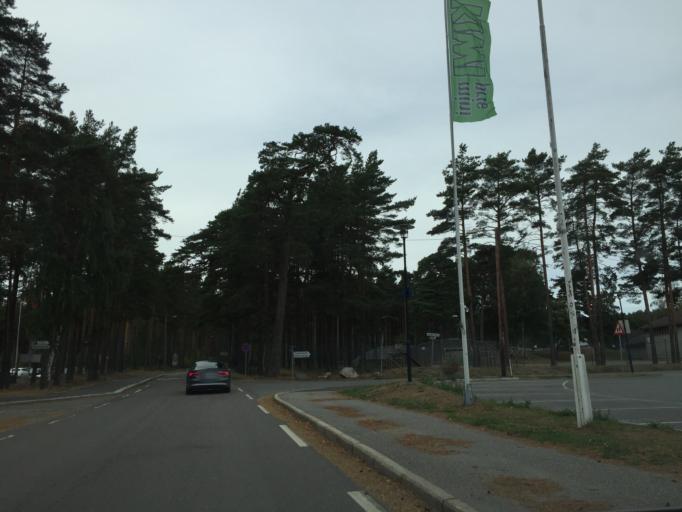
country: NO
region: Ostfold
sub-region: Hvaler
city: Skjaerhalden
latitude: 59.0281
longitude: 11.0324
